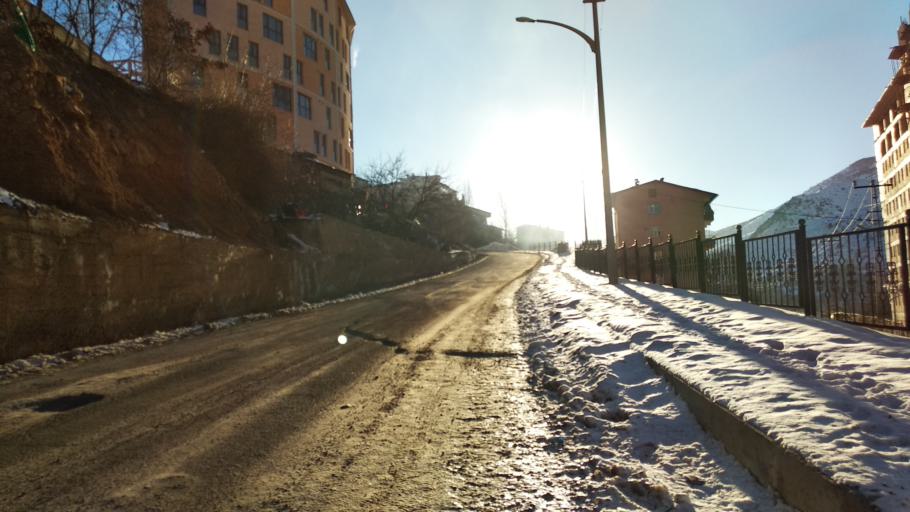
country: TR
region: Gumushane
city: Gumushkhane
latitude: 40.4383
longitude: 39.5068
